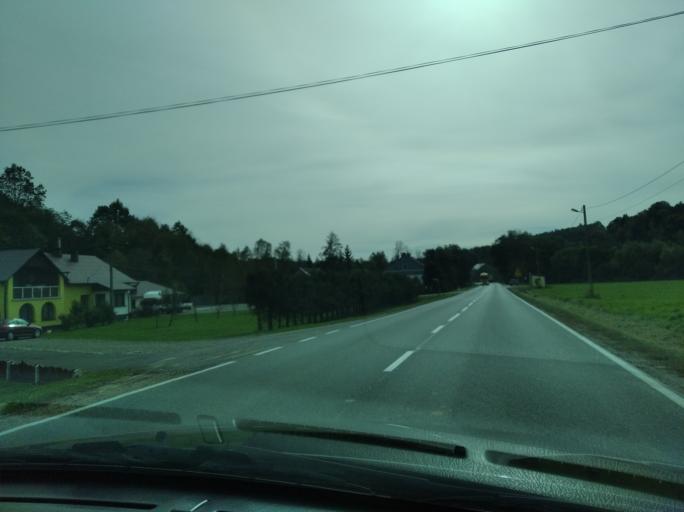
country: PL
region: Subcarpathian Voivodeship
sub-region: Powiat strzyzowski
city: Wisniowa
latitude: 49.8915
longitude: 21.6438
